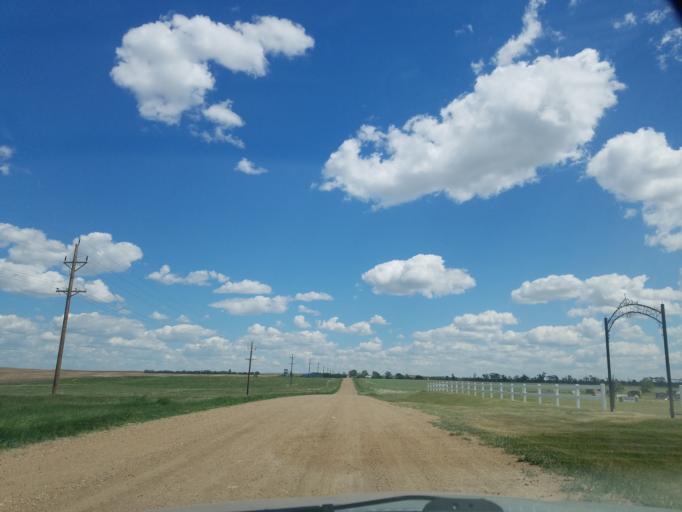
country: US
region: North Dakota
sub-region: McKenzie County
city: Watford City
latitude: 47.8194
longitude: -103.5593
